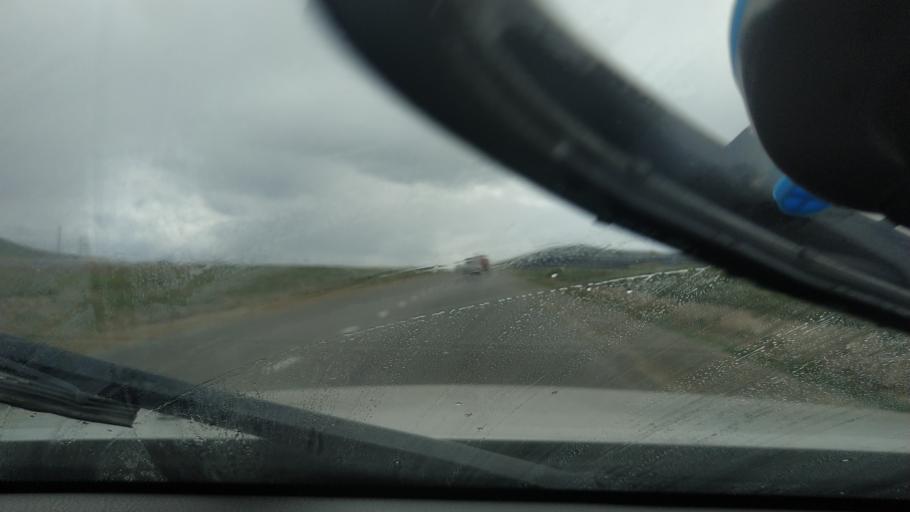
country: MN
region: Ulaanbaatar
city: Ulaanbaatar
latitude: 47.8057
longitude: 106.7495
